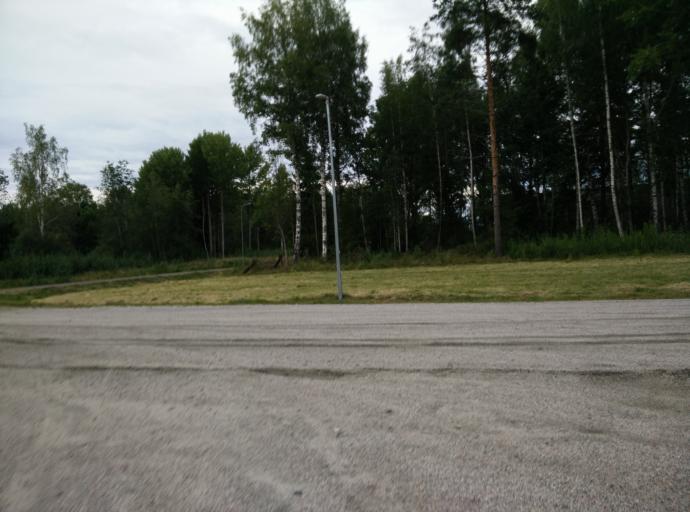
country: FI
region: Haeme
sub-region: Haemeenlinna
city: Haemeenlinna
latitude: 60.9859
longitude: 24.4807
